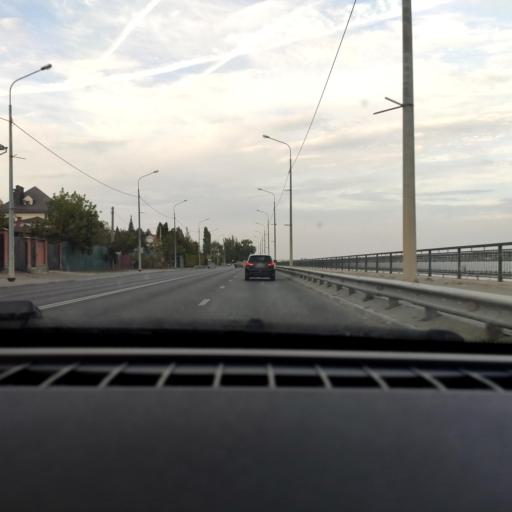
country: RU
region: Voronezj
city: Voronezh
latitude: 51.6751
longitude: 39.2257
